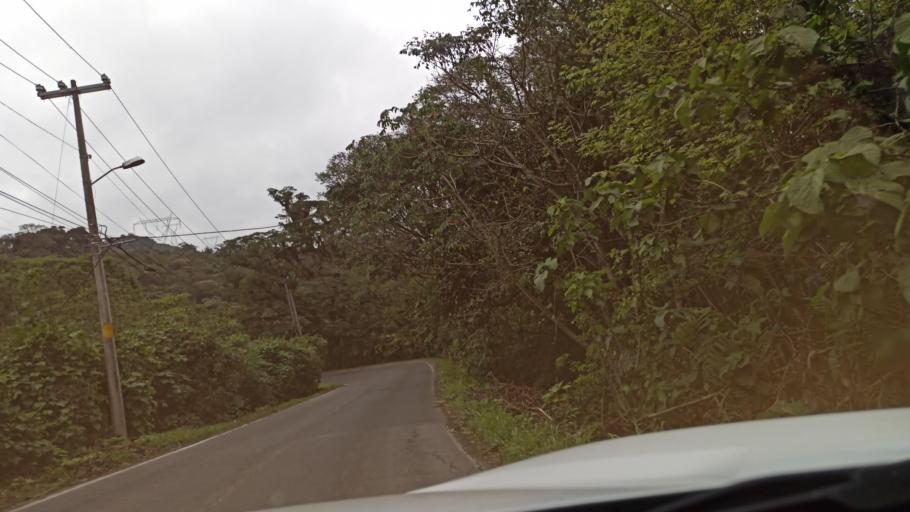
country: MX
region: Veracruz
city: Cuautlapan
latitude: 18.8910
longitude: -97.0143
